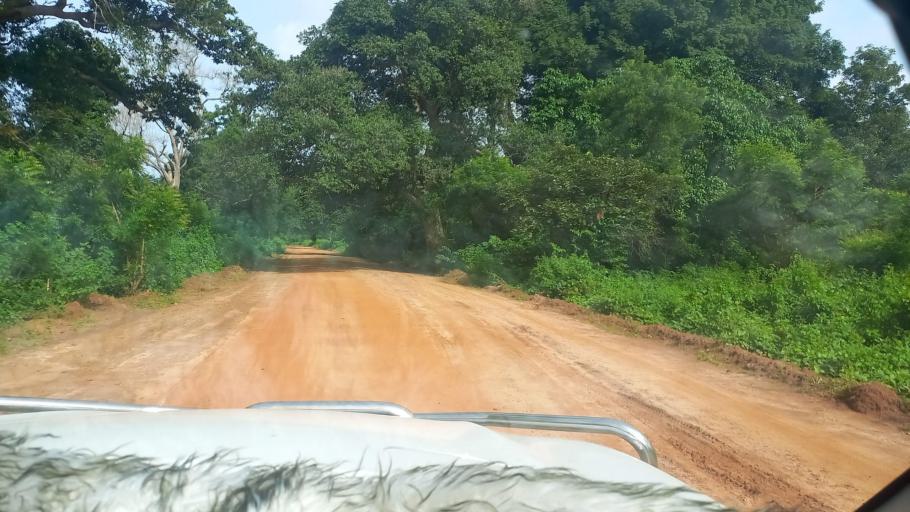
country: SN
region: Ziguinchor
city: Ziguinchor
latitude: 12.6672
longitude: -16.2671
